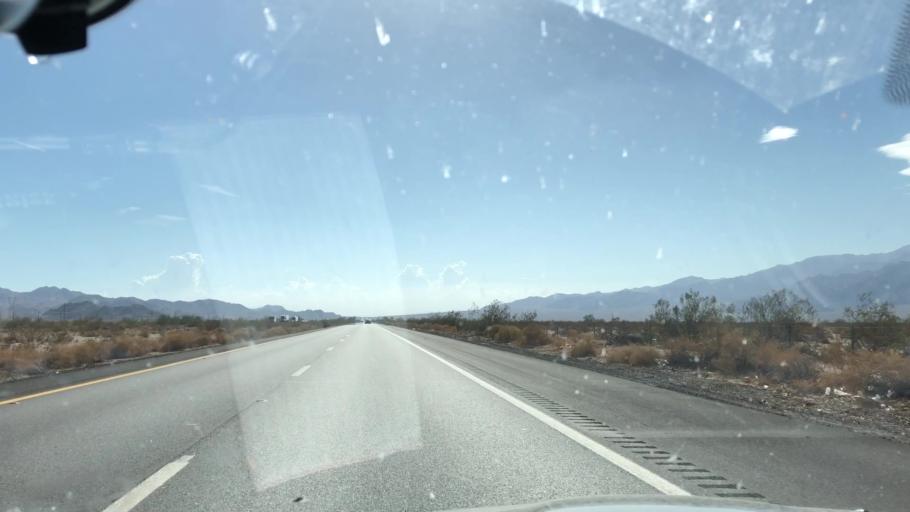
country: US
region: California
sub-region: Imperial County
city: Niland
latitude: 33.6735
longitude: -115.5857
